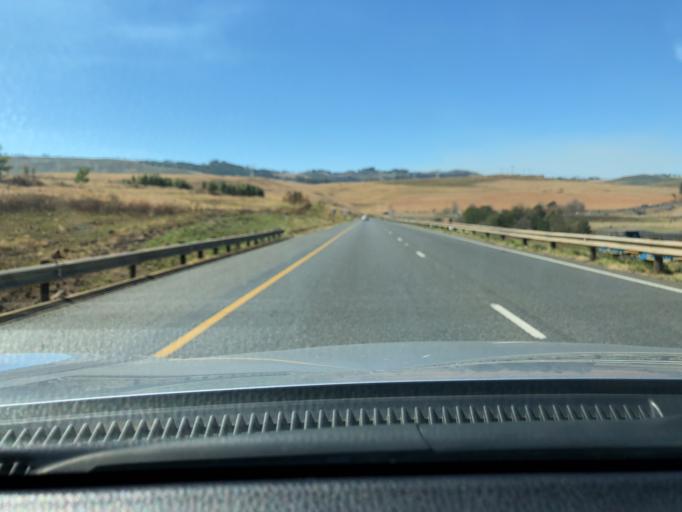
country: ZA
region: KwaZulu-Natal
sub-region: uMgungundlovu District Municipality
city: Howick
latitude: -29.4165
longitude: 30.1583
